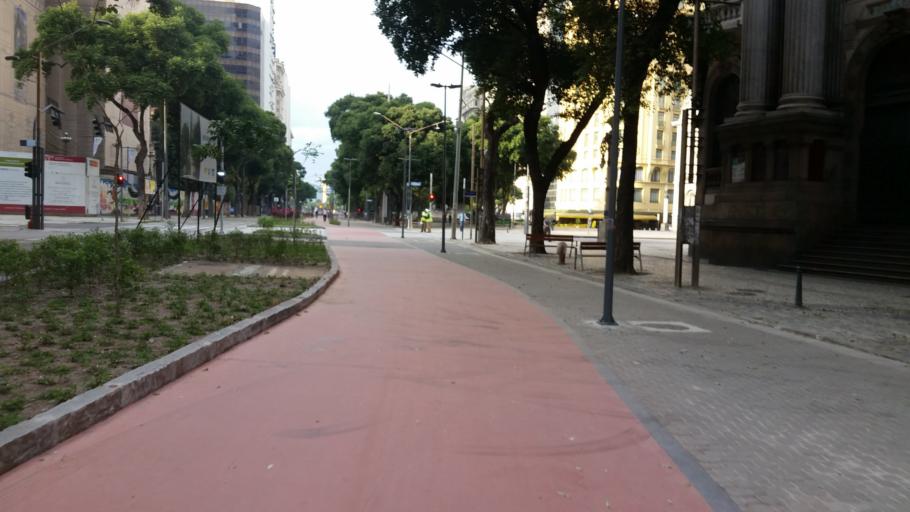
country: BR
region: Rio de Janeiro
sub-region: Rio De Janeiro
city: Rio de Janeiro
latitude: -22.9090
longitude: -43.1763
